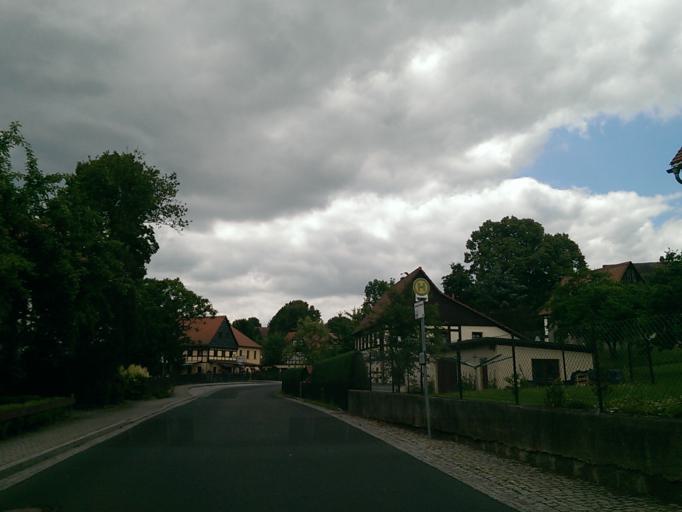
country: DE
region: Saxony
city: Bertsdorf-Hoernitz
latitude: 50.8905
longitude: 14.7446
